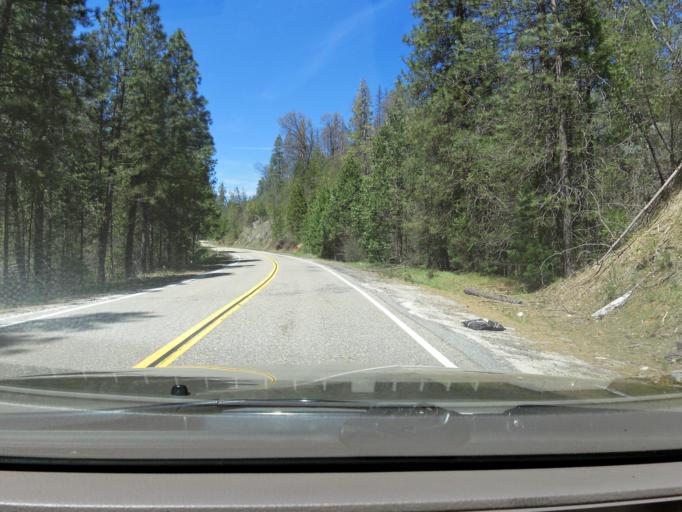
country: US
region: California
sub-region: Madera County
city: Oakhurst
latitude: 37.2807
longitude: -119.5763
